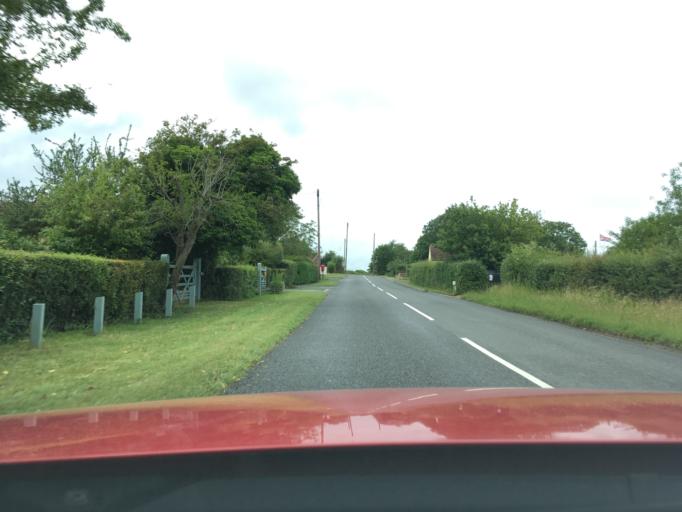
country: GB
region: England
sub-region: Worcestershire
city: Evesham
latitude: 52.0555
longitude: -1.9359
